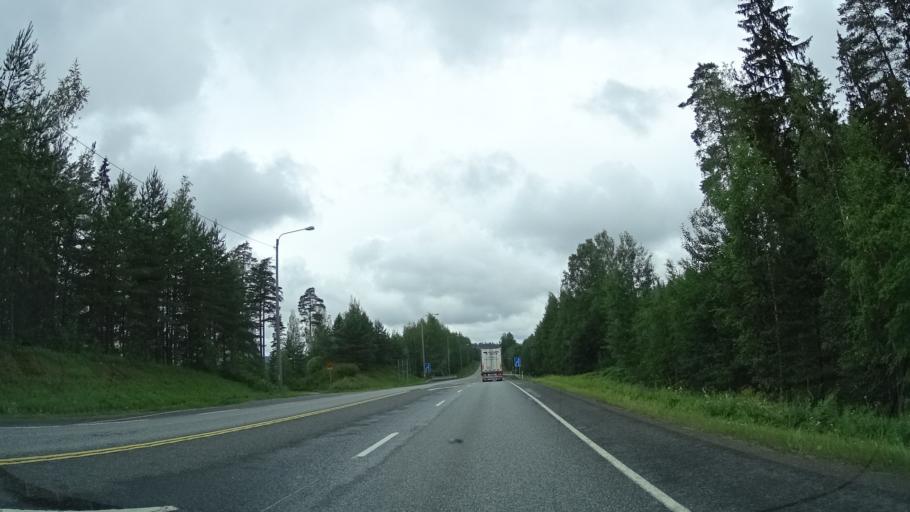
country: FI
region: Uusimaa
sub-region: Helsinki
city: Karkkila
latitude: 60.5403
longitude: 24.2289
